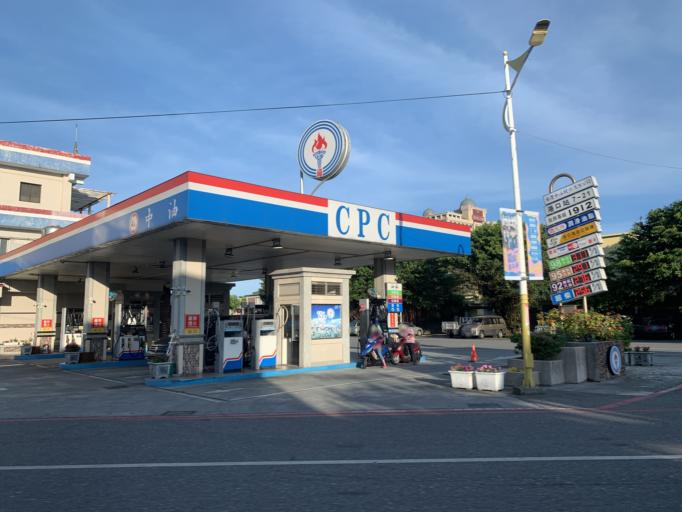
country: TW
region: Taiwan
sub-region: Hualien
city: Hualian
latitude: 23.9975
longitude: 121.6310
